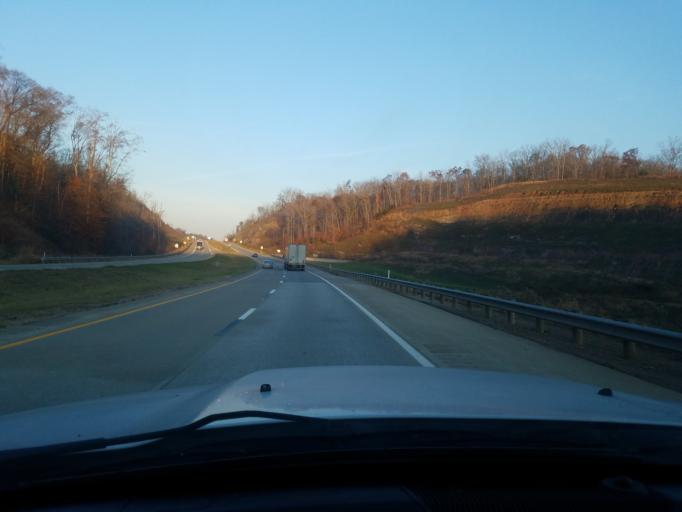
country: US
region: West Virginia
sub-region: Putnam County
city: Eleanor
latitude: 38.5248
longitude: -81.9362
